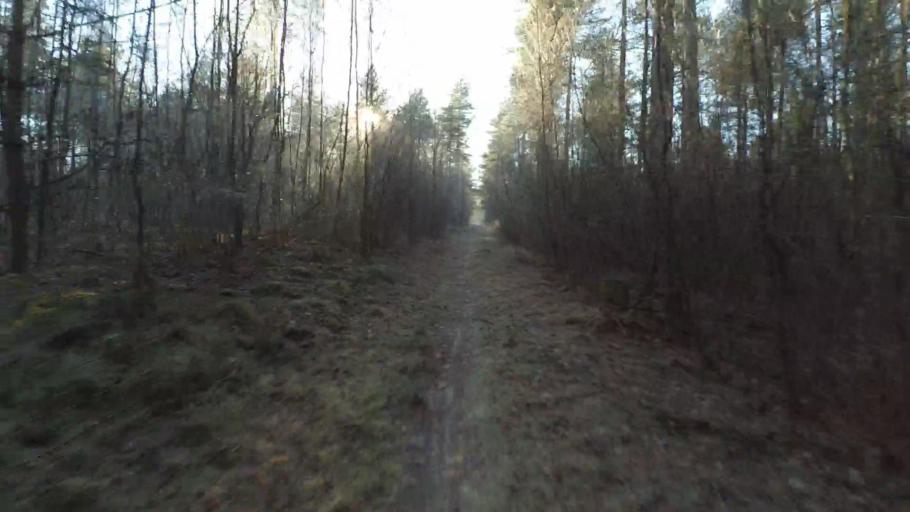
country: NL
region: Utrecht
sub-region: Gemeente Amersfoort
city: Amersfoort
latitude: 52.1124
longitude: 5.3671
